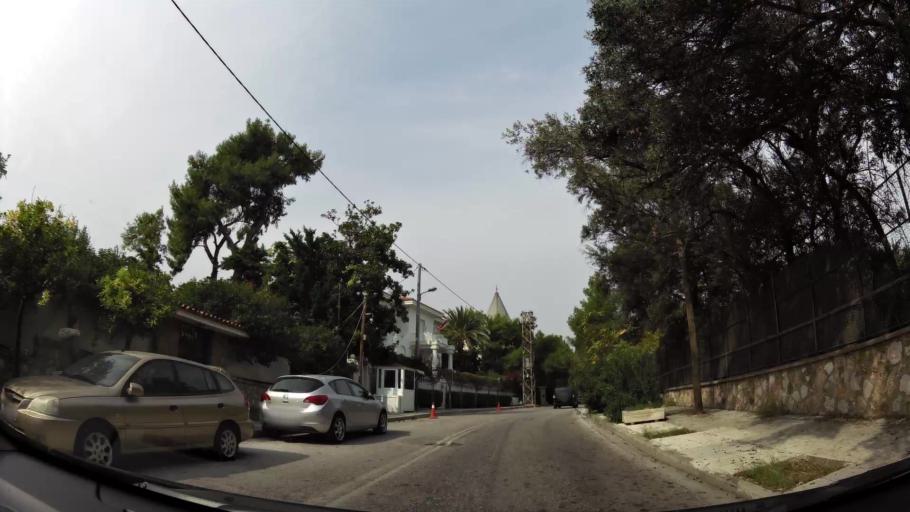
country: GR
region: Attica
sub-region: Nomarchia Athinas
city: Psychiko
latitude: 38.0069
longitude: 23.7726
